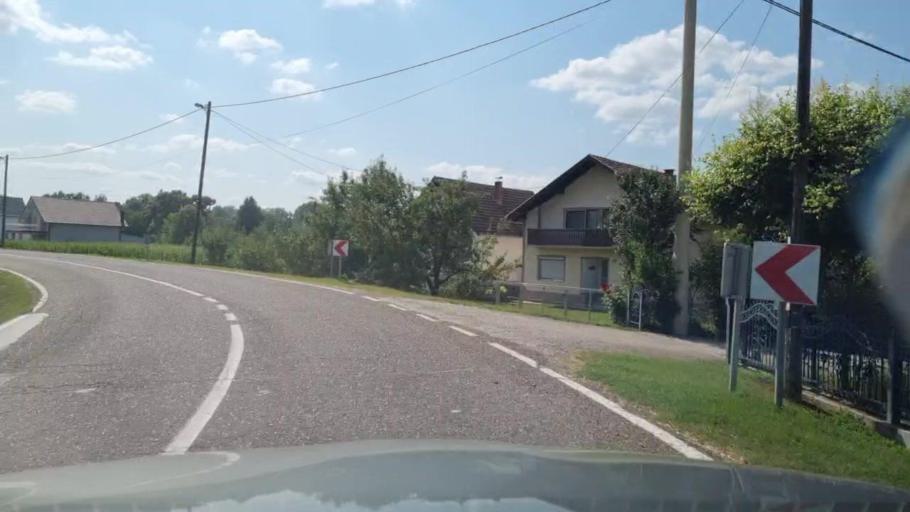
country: BA
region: Federation of Bosnia and Herzegovina
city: Donja Dubica
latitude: 45.0703
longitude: 18.4373
